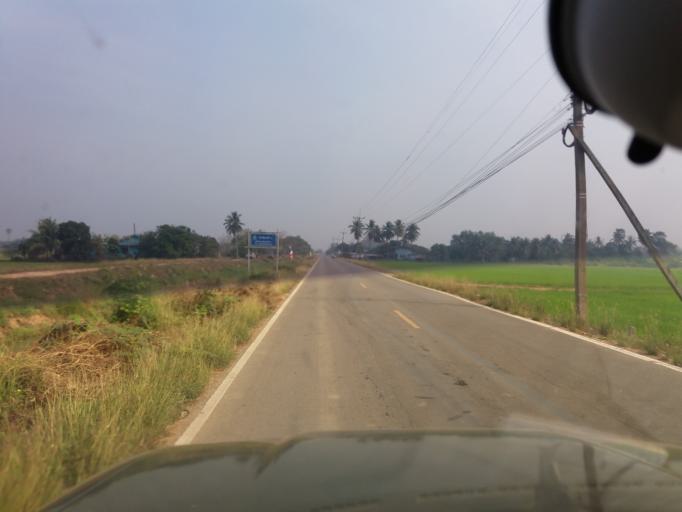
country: TH
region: Suphan Buri
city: Doem Bang Nang Buat
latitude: 14.8825
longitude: 100.1797
